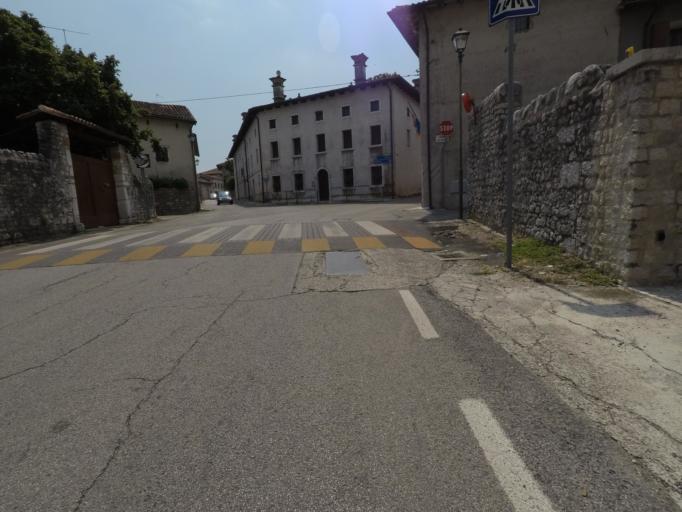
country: IT
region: Friuli Venezia Giulia
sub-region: Provincia di Pordenone
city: Aviano-Castello
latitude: 46.0512
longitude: 12.5642
